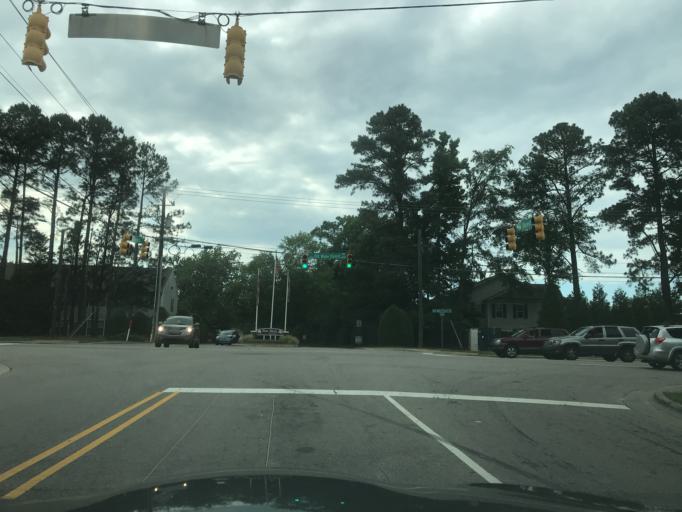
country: US
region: North Carolina
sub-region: Wake County
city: Raleigh
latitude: 35.8654
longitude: -78.5917
